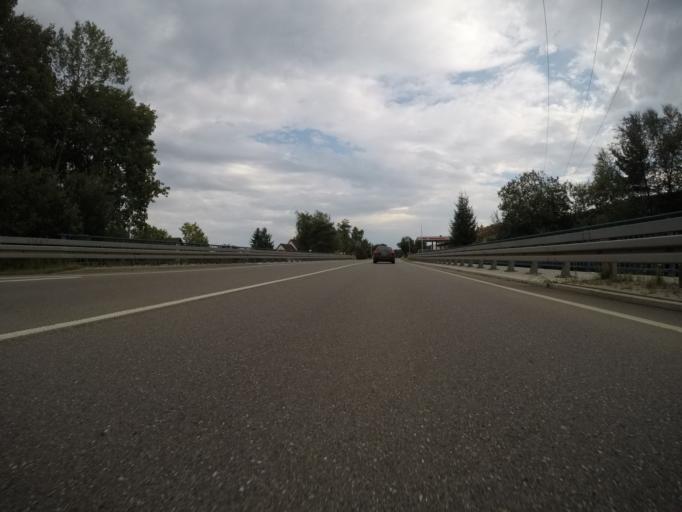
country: DE
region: Baden-Wuerttemberg
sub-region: Freiburg Region
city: Monchweiler
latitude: 48.1058
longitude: 8.4155
